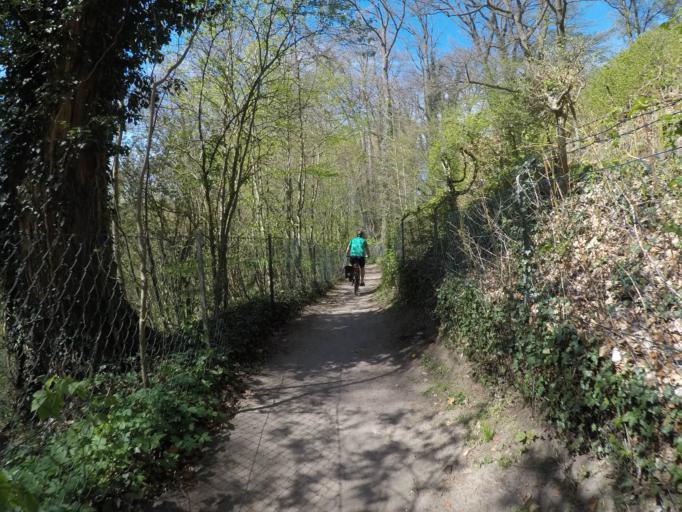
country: DE
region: Hamburg
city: Poppenbuettel
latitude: 53.6716
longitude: 10.0981
